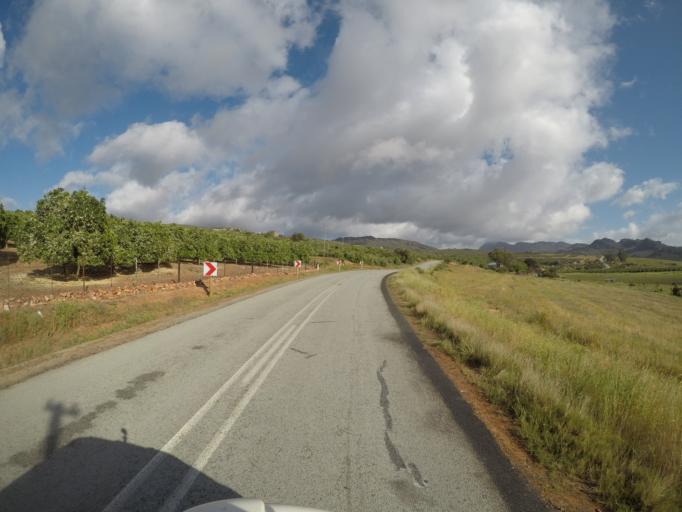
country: ZA
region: Western Cape
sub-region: West Coast District Municipality
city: Clanwilliam
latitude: -32.4380
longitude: 18.9414
